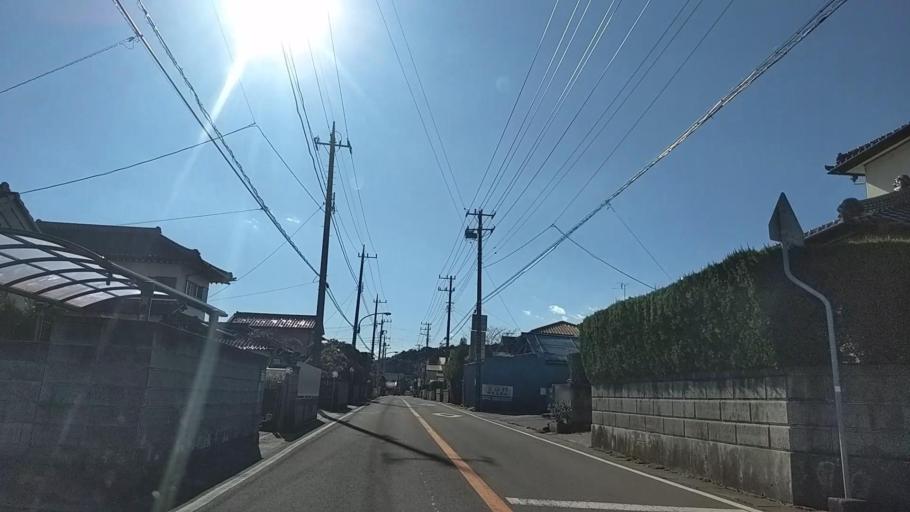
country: JP
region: Chiba
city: Tateyama
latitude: 34.9792
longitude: 139.8632
